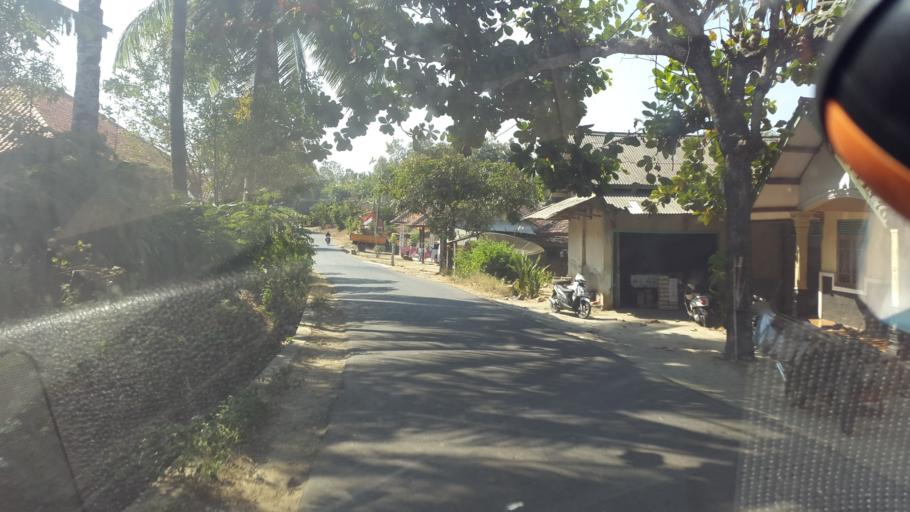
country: ID
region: West Java
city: Simpang
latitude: -7.3592
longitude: 106.4530
